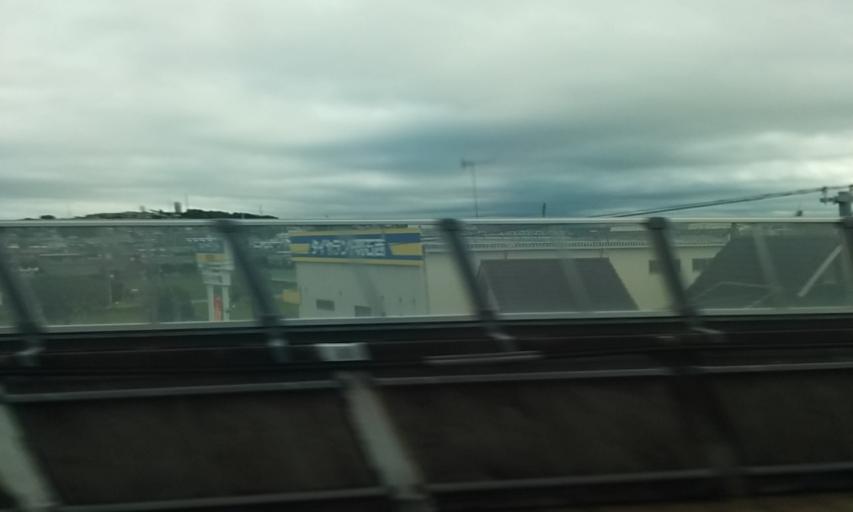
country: JP
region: Hyogo
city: Akashi
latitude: 34.6849
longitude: 134.9194
